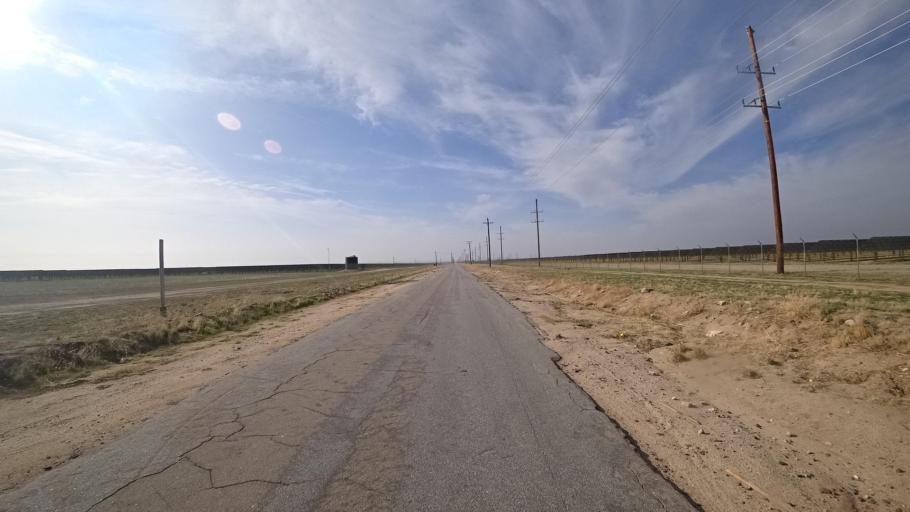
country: US
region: California
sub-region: Kern County
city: Arvin
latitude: 35.3261
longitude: -118.8168
